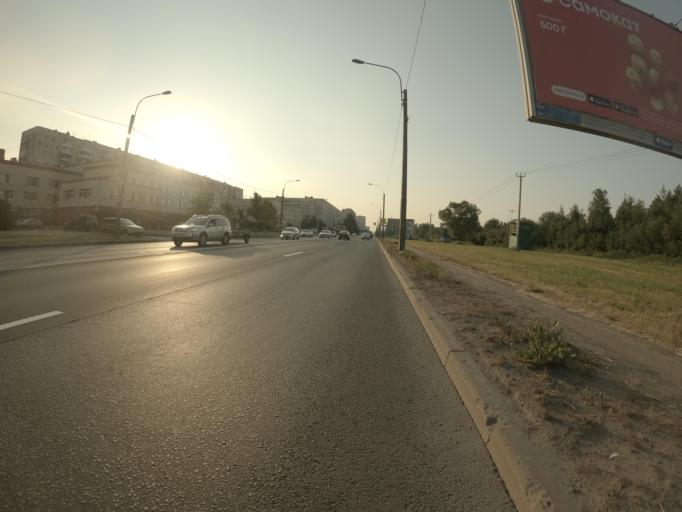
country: RU
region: St.-Petersburg
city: Krasnogvargeisky
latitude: 59.9500
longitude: 30.5014
